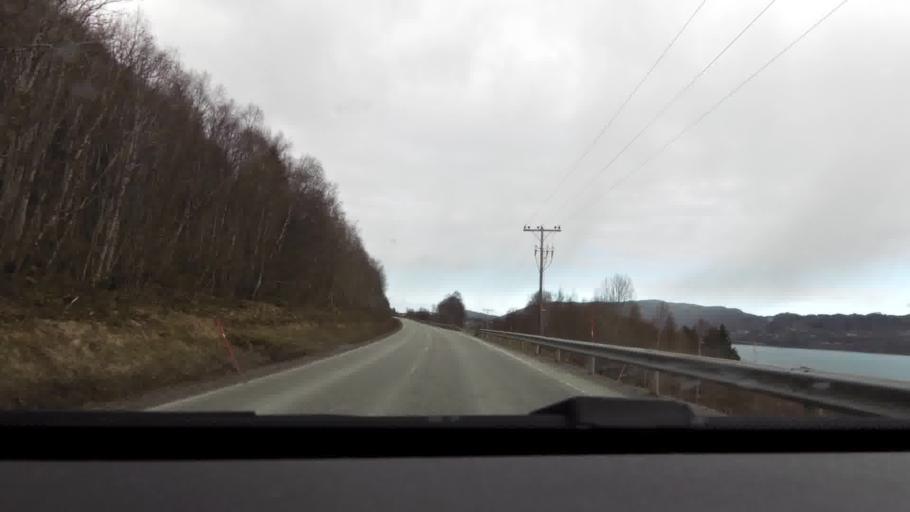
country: NO
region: More og Romsdal
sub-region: Eide
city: Eide
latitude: 62.9402
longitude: 7.4298
